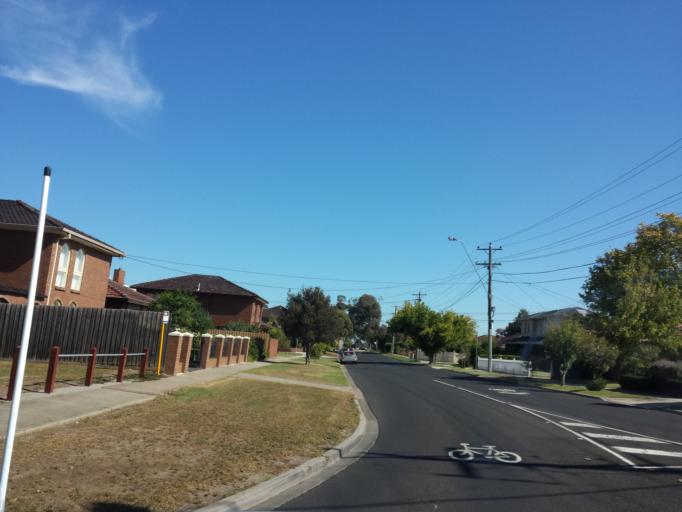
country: AU
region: Victoria
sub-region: Moonee Valley
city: Essendon West
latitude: -37.7494
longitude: 144.8716
